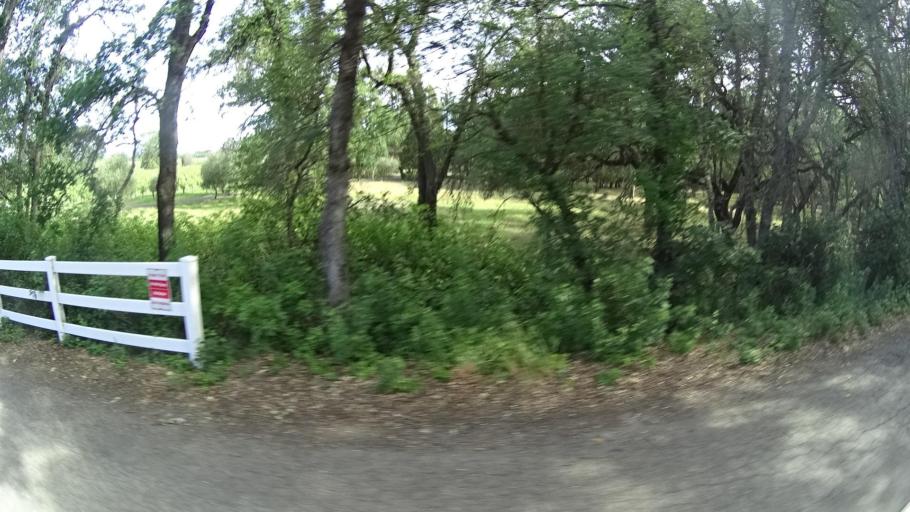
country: US
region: California
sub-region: Lake County
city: Kelseyville
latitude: 38.9825
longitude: -122.8610
